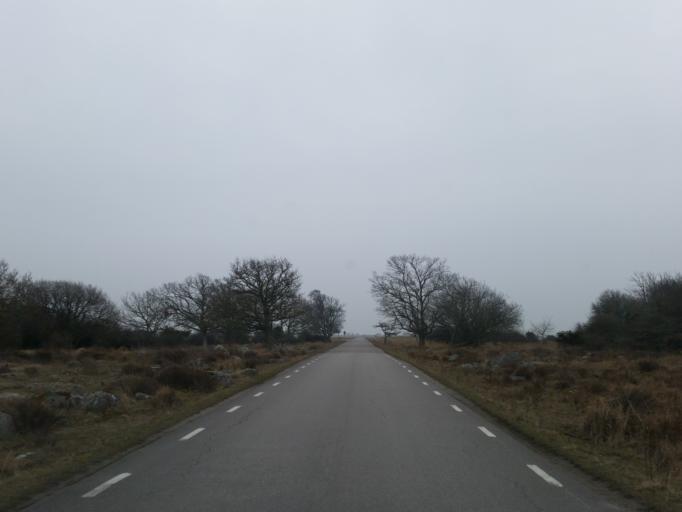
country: SE
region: Kalmar
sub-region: Morbylanga Kommun
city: Moerbylanga
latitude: 56.2135
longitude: 16.4074
